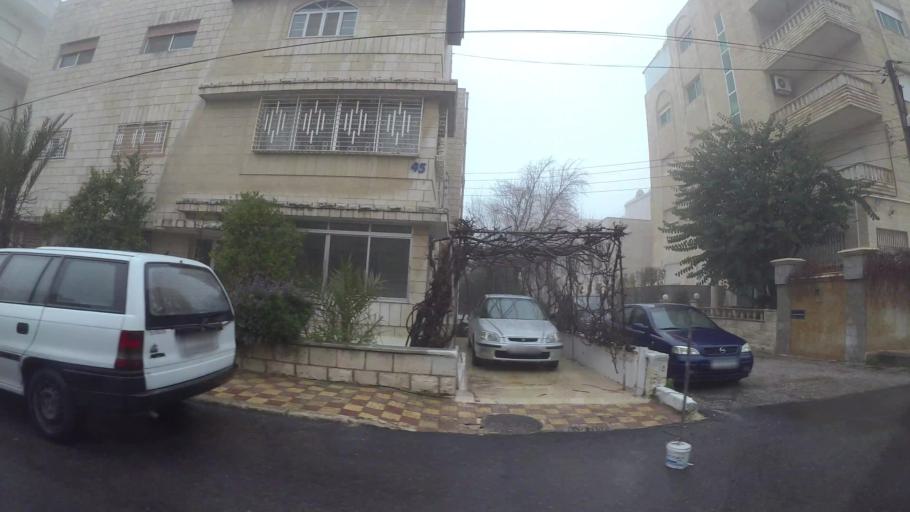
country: JO
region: Amman
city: Wadi as Sir
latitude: 31.9629
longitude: 35.8721
